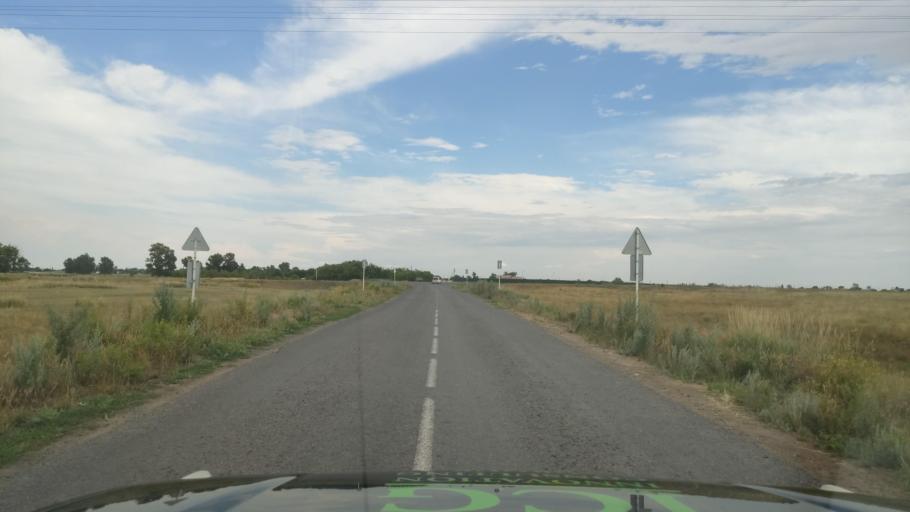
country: KZ
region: Pavlodar
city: Pavlodar
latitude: 52.6612
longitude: 77.4938
